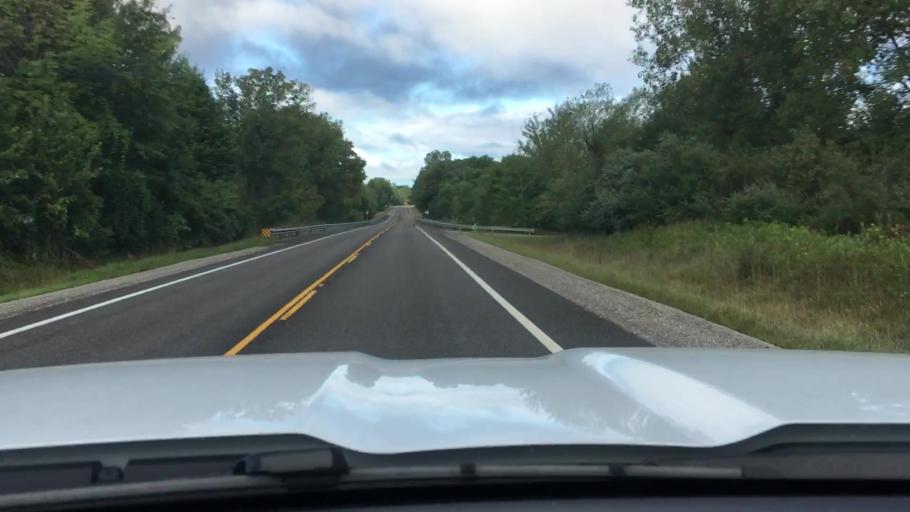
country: US
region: Michigan
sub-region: Tuscola County
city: Caro
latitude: 43.3436
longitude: -83.3646
